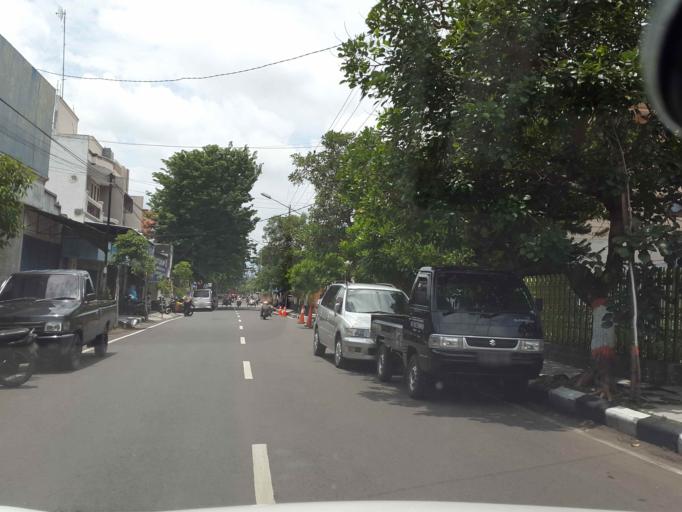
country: ID
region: East Java
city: Mojokerto
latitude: -7.4618
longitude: 112.4353
